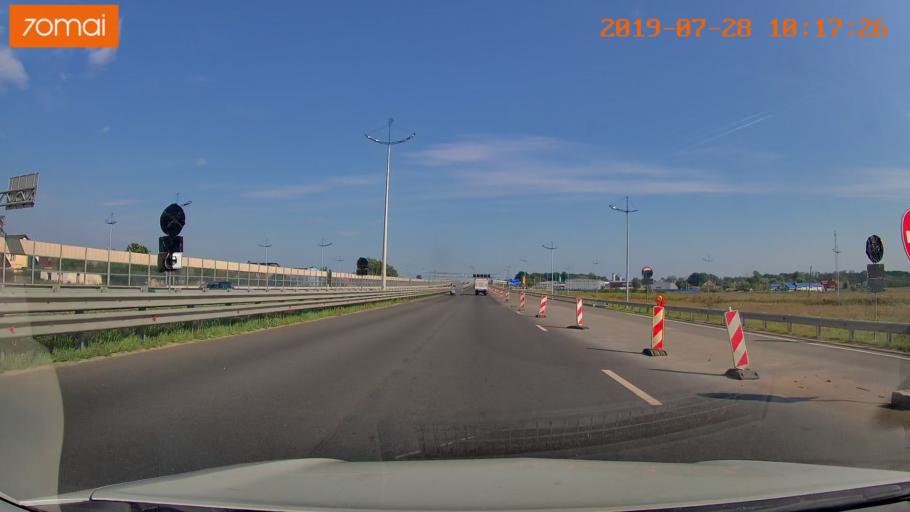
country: RU
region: Kaliningrad
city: Maloye Isakovo
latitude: 54.7398
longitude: 20.5944
